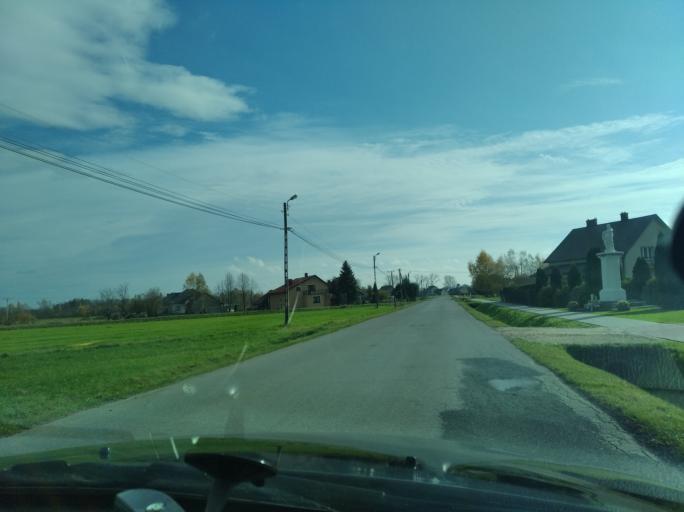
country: PL
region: Subcarpathian Voivodeship
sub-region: Powiat ropczycko-sedziszowski
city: Ostrow
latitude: 50.0981
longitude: 21.6351
